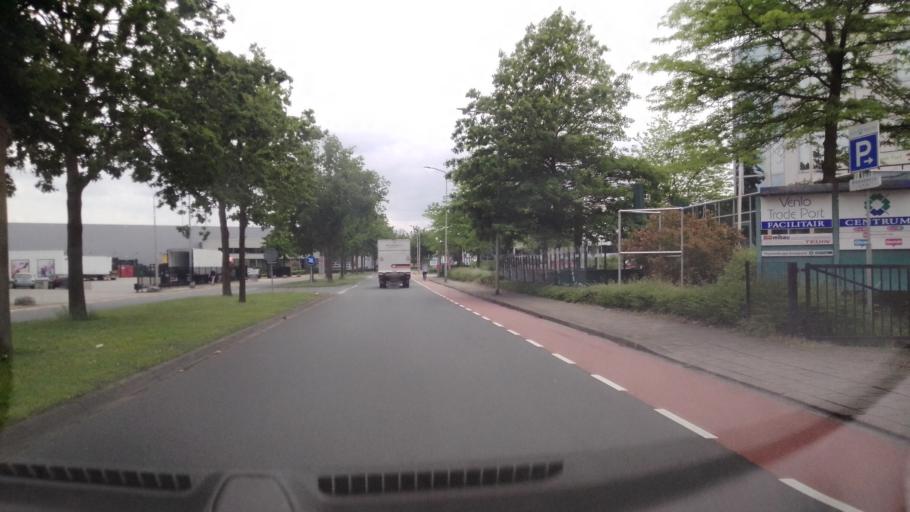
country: NL
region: Limburg
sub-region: Gemeente Venlo
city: Venlo
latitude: 51.3918
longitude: 6.1332
